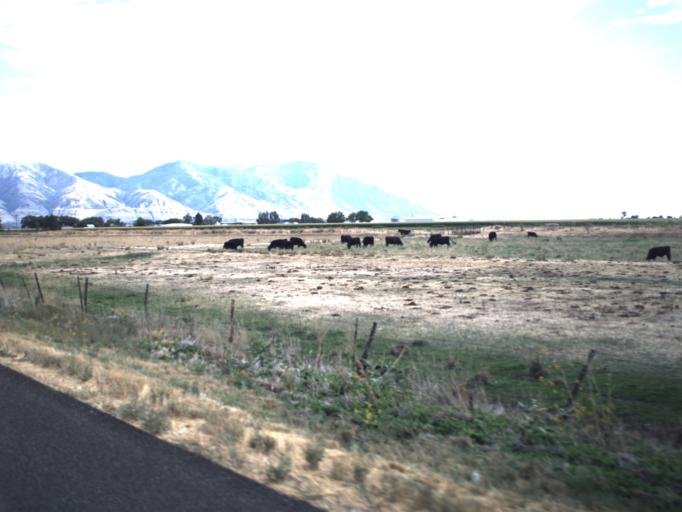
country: US
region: Utah
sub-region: Box Elder County
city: Honeyville
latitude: 41.5564
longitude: -112.1350
